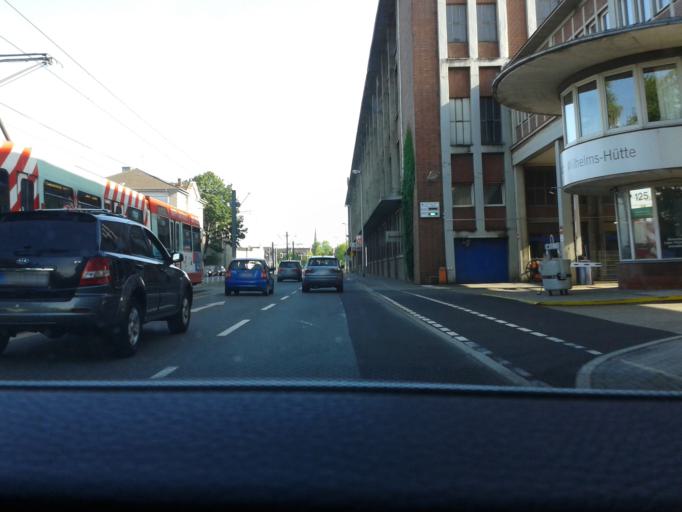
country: DE
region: North Rhine-Westphalia
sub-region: Regierungsbezirk Dusseldorf
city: Muelheim (Ruhr)
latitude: 51.4348
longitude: 6.8752
